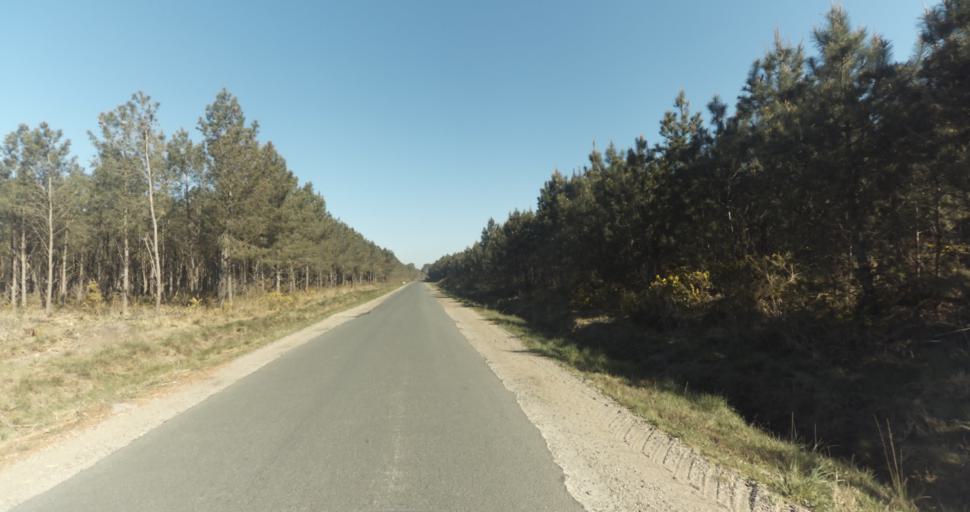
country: FR
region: Aquitaine
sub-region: Departement de la Gironde
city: Marcheprime
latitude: 44.7522
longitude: -0.8486
